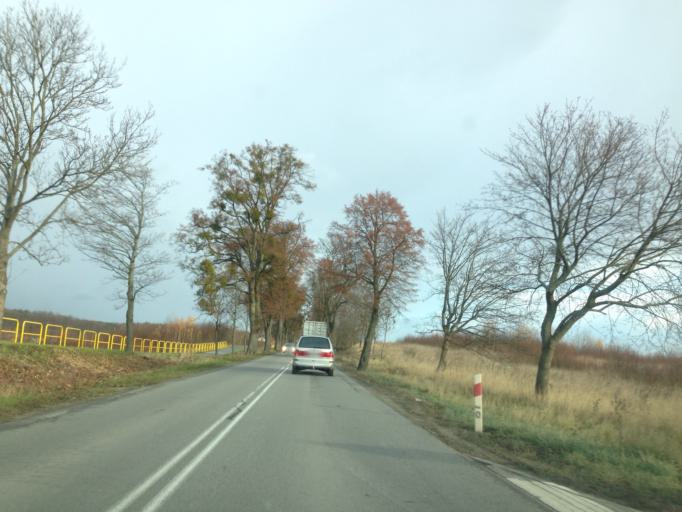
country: PL
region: Pomeranian Voivodeship
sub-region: Powiat gdanski
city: Kowale
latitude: 54.2962
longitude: 18.5350
